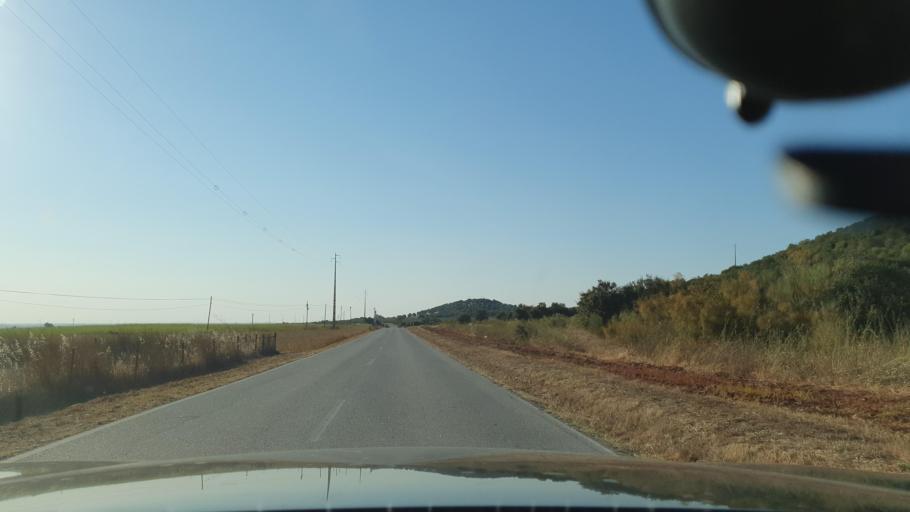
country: PT
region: Evora
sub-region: Estremoz
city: Estremoz
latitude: 38.8853
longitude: -7.6478
